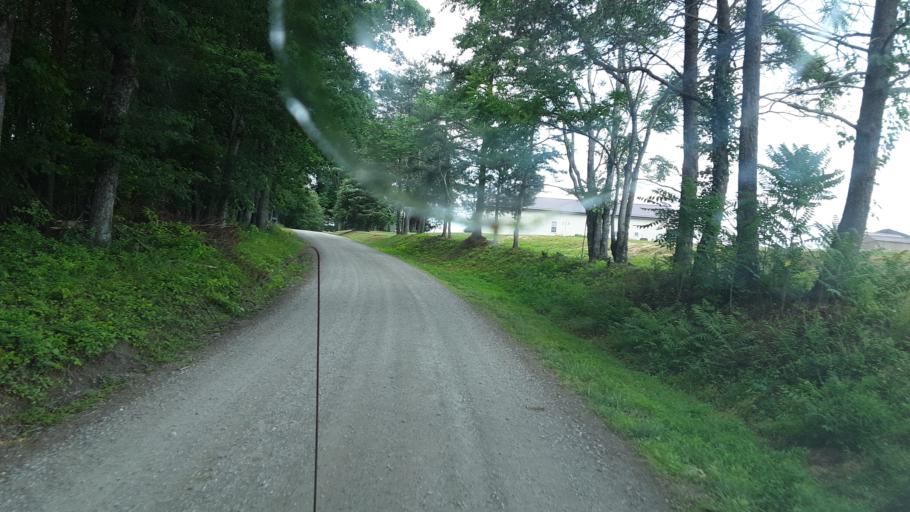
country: US
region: Virginia
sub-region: Pittsylvania County
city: Chatham
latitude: 36.8541
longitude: -79.4397
